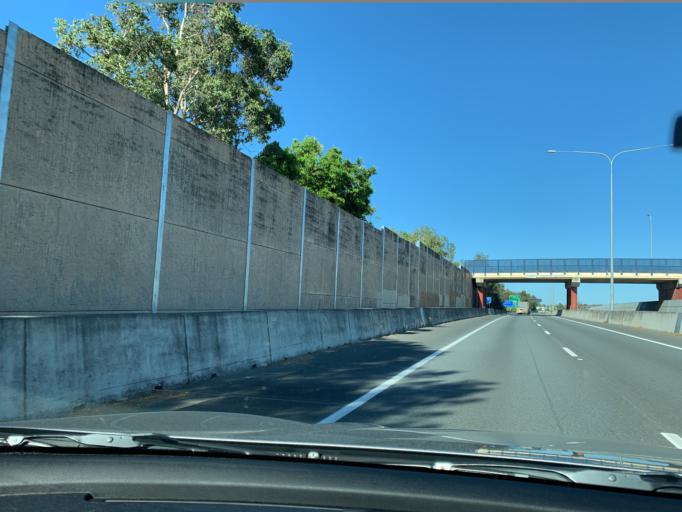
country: AU
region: Queensland
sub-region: Brisbane
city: Wynnum West
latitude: -27.4476
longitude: 153.1252
